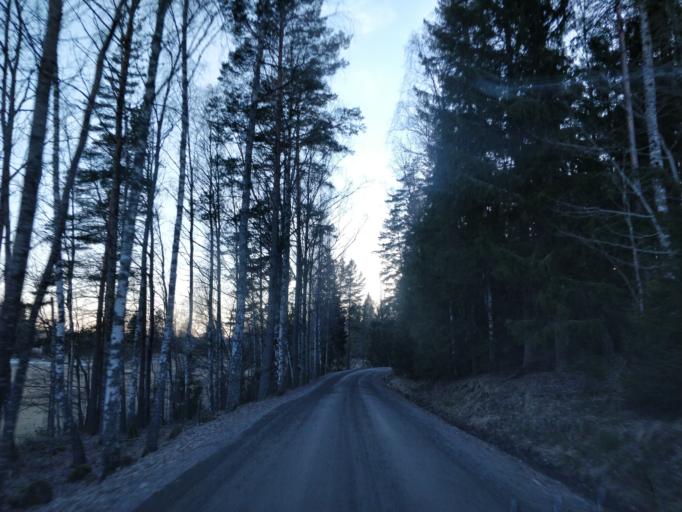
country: SE
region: Uppsala
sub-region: Enkopings Kommun
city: Orsundsbro
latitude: 59.8273
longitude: 17.1642
